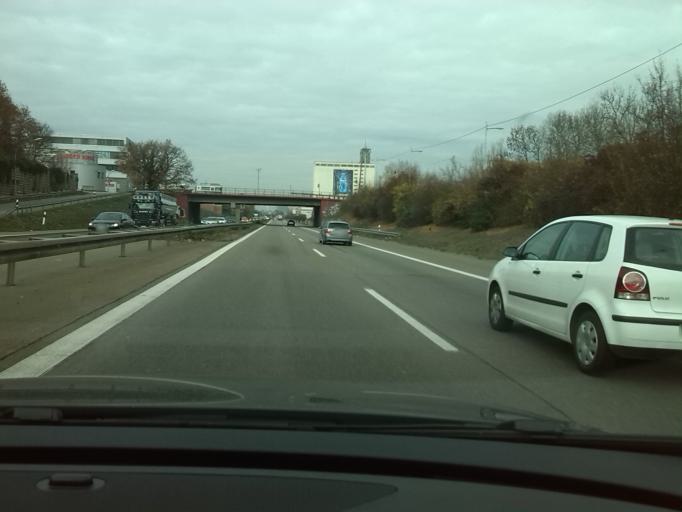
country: DE
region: Baden-Wuerttemberg
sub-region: Regierungsbezirk Stuttgart
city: Ostfildern
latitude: 48.7594
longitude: 9.2579
